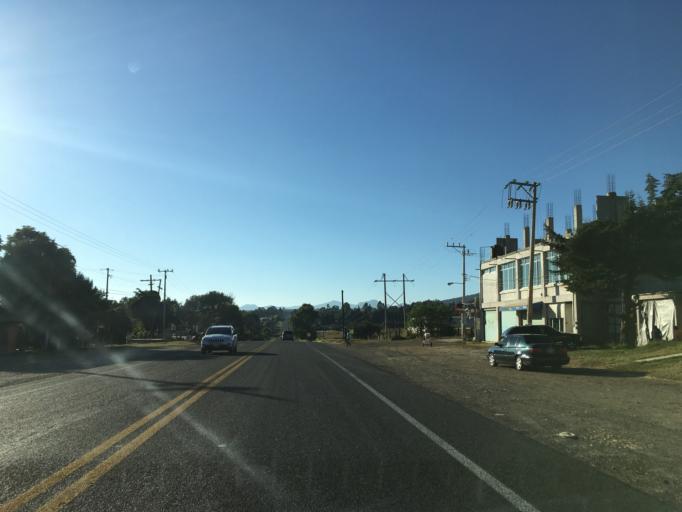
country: MX
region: Michoacan
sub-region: Zitacuaro
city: Puentecillas (Tercera Manzana de Zirahuato)
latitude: 19.4852
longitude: -100.3976
